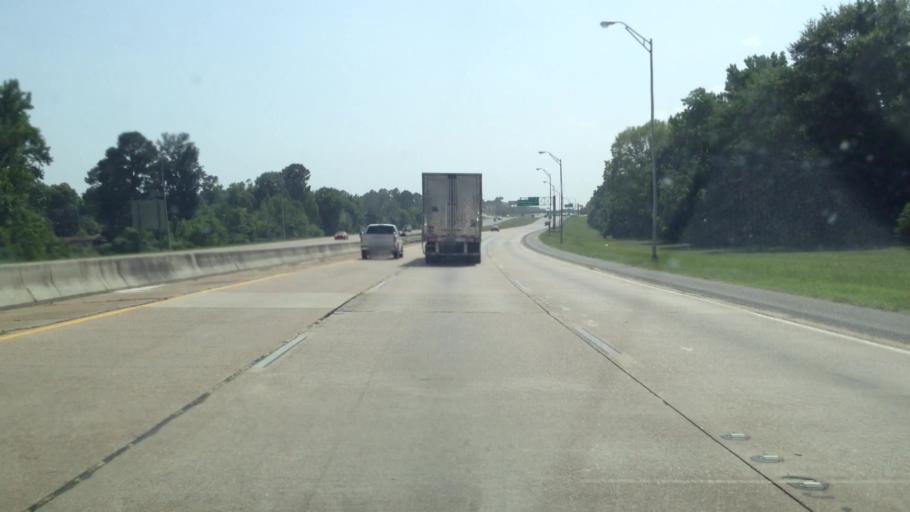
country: US
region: Louisiana
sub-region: Caddo Parish
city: Shreveport
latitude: 32.4649
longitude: -93.8179
